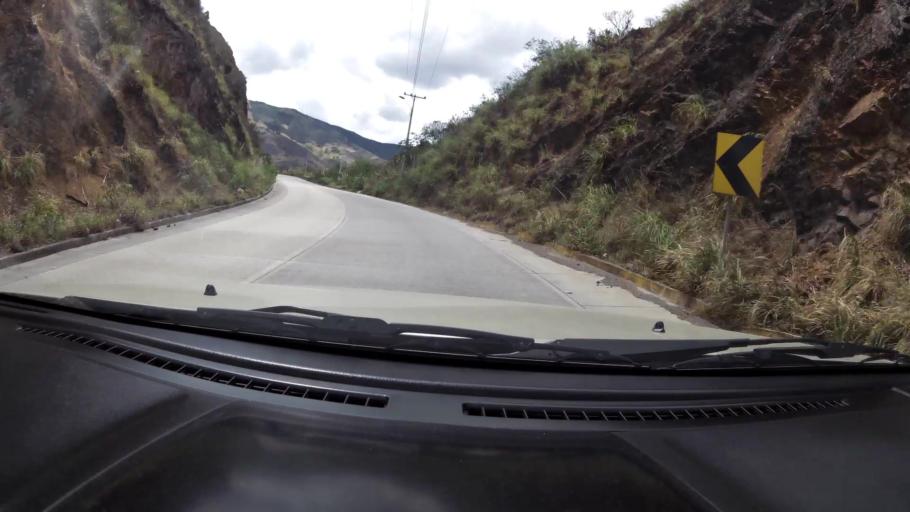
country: EC
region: Azuay
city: Cuenca
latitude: -3.1442
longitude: -79.1262
